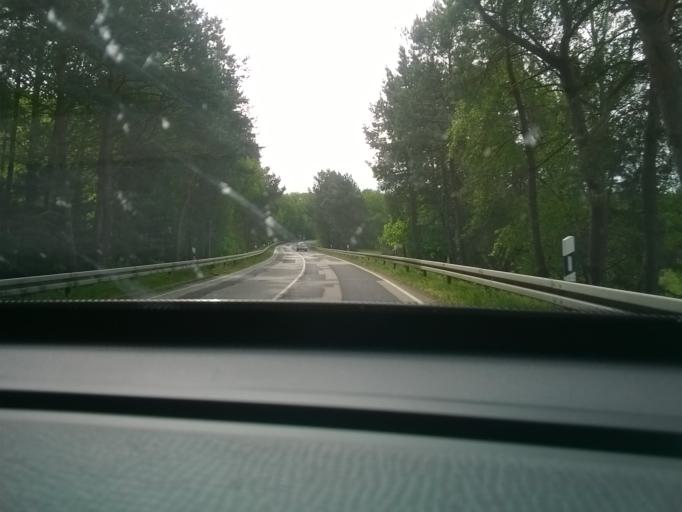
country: DE
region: Brandenburg
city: Wittstock
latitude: 53.1015
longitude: 12.4834
